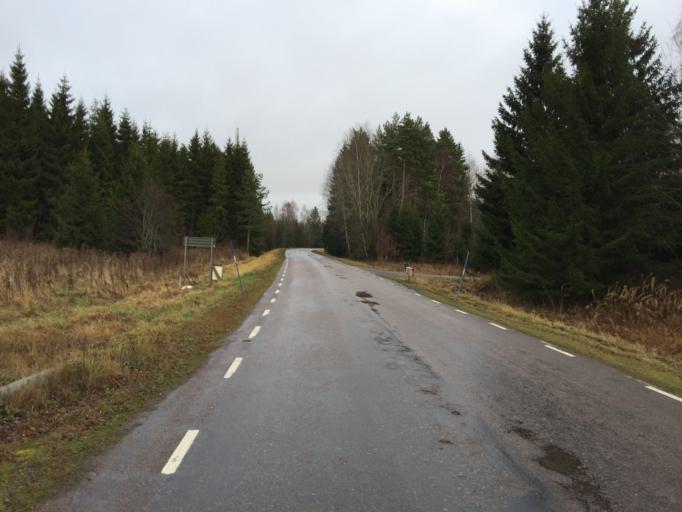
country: SE
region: Uppsala
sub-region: Osthammars Kommun
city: Bjorklinge
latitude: 60.0543
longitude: 17.5368
